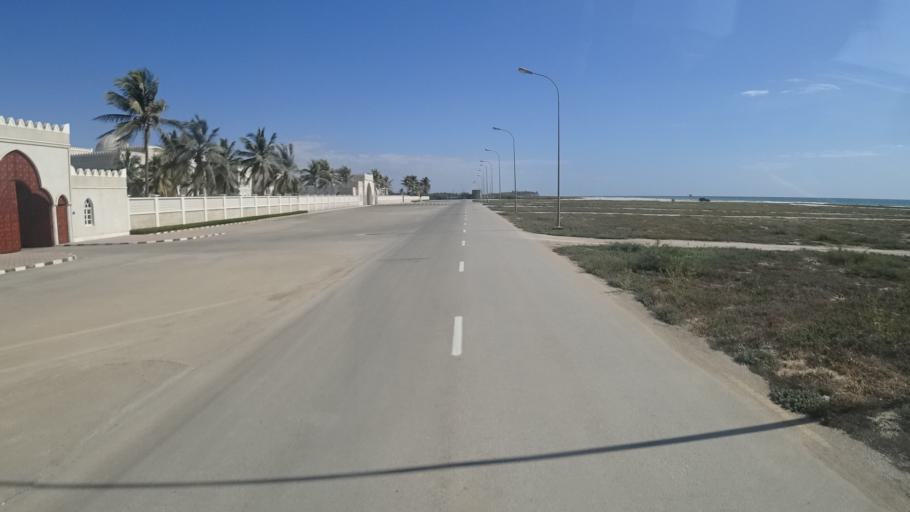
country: OM
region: Zufar
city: Salalah
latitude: 16.9946
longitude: 54.0624
